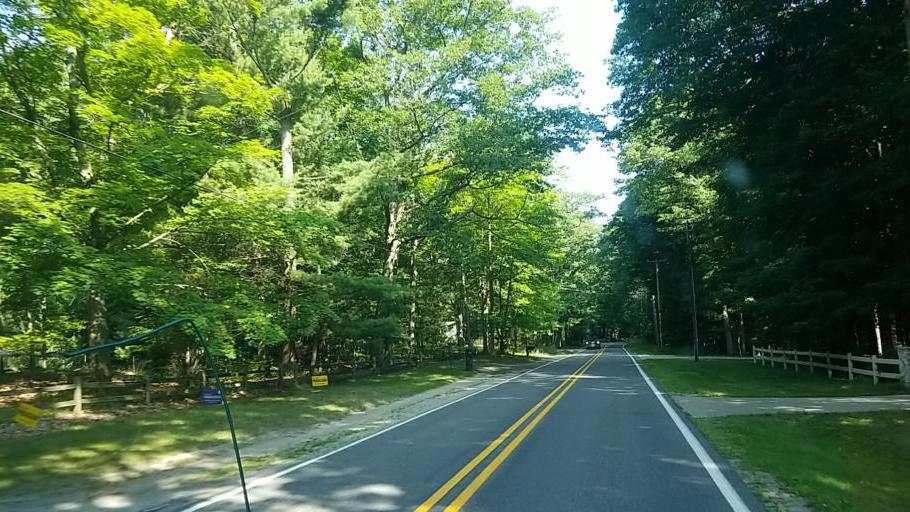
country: US
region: Michigan
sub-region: Muskegon County
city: Whitehall
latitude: 43.3190
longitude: -86.3945
